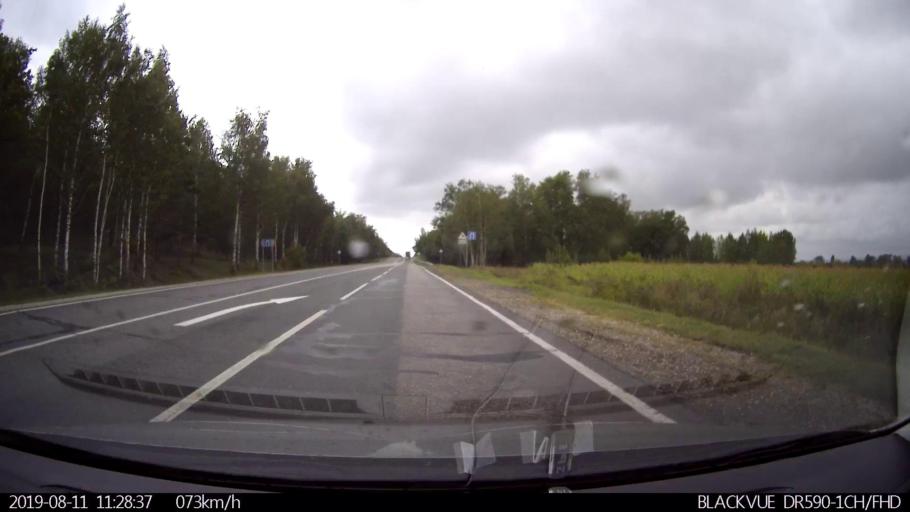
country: RU
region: Ulyanovsk
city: Krasnyy Gulyay
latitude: 54.0805
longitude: 48.2294
